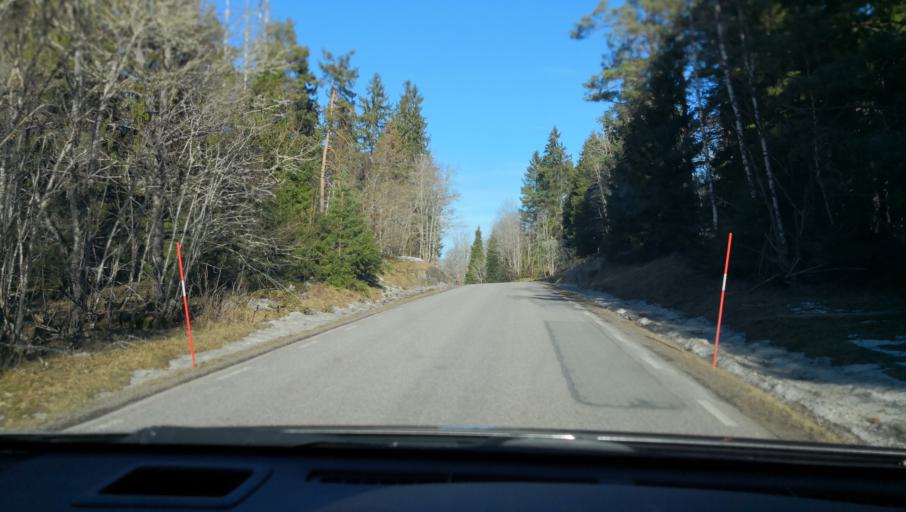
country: SE
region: Uppsala
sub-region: Osthammars Kommun
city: Osterbybruk
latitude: 60.2157
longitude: 17.9077
